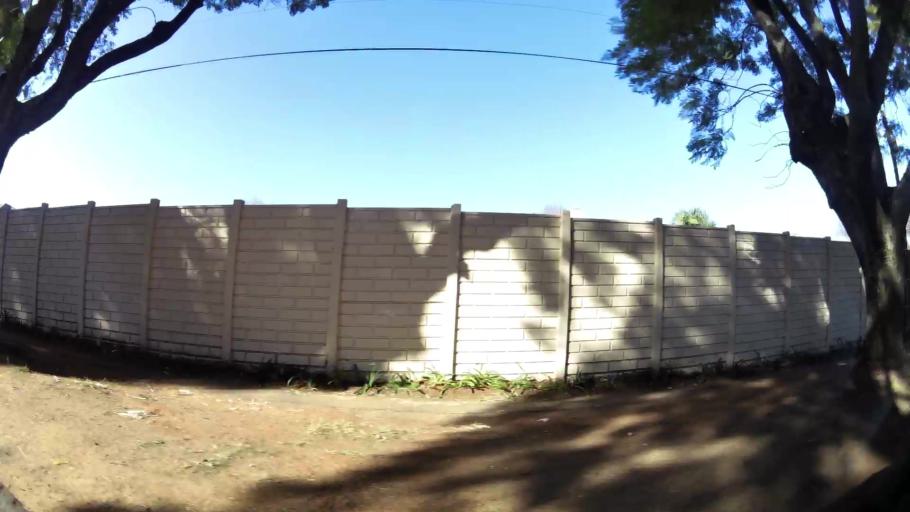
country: ZA
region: Gauteng
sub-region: City of Johannesburg Metropolitan Municipality
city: Johannesburg
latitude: -26.1458
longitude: 28.0887
